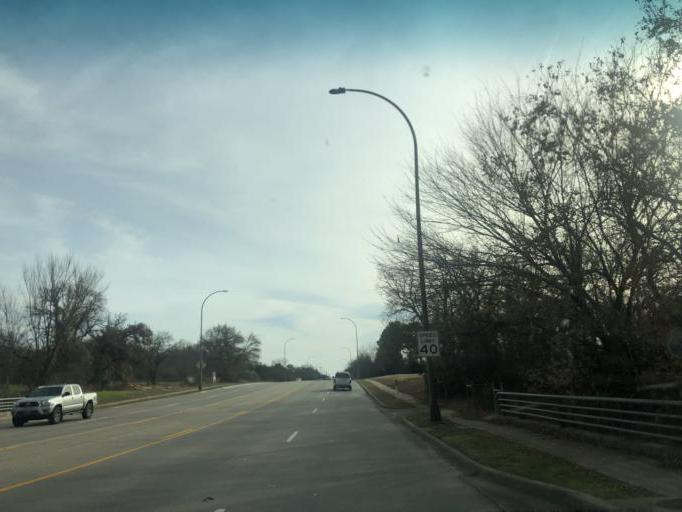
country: US
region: Texas
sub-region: Tarrant County
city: Dalworthington Gardens
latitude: 32.6919
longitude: -97.1494
